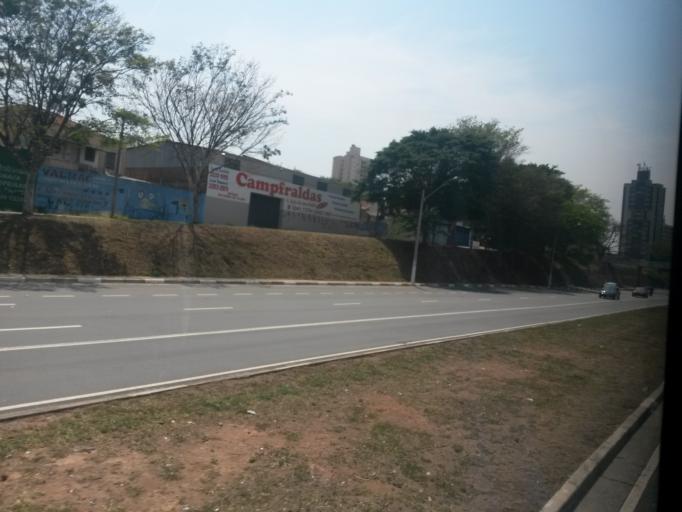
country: BR
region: Sao Paulo
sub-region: Campinas
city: Campinas
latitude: -22.8996
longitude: -47.0872
